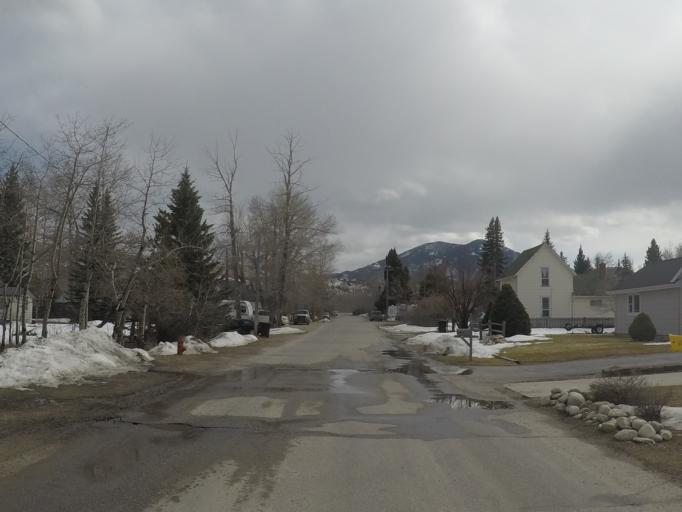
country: US
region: Montana
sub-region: Carbon County
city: Red Lodge
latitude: 45.1769
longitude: -109.2506
